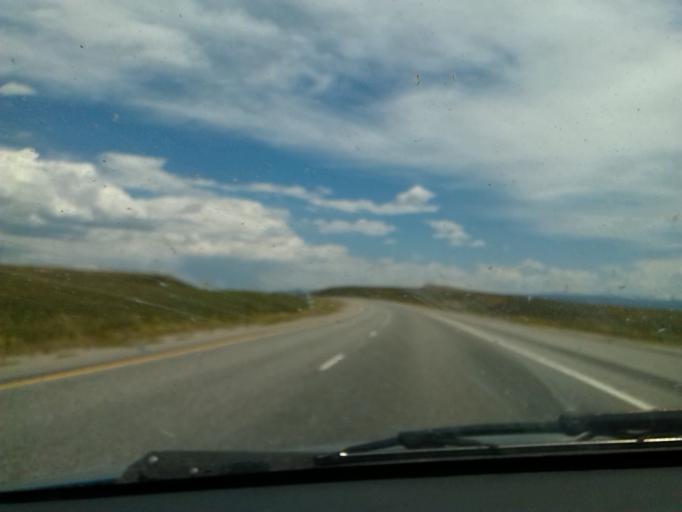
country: US
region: Wyoming
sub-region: Carbon County
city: Saratoga
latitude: 41.7368
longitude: -106.4904
